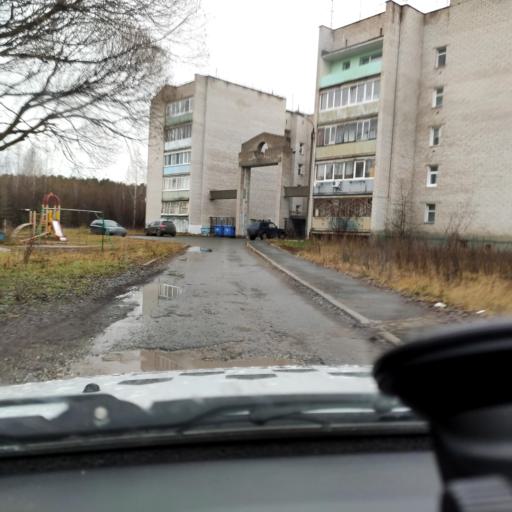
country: RU
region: Perm
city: Perm
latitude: 58.0566
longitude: 56.2814
